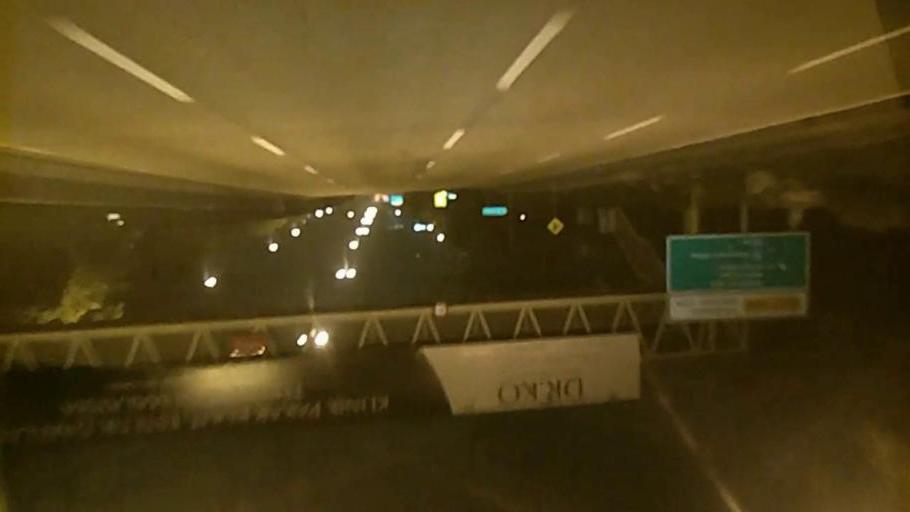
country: MY
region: Selangor
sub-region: Petaling
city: Petaling Jaya
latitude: 3.1387
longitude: 101.6241
